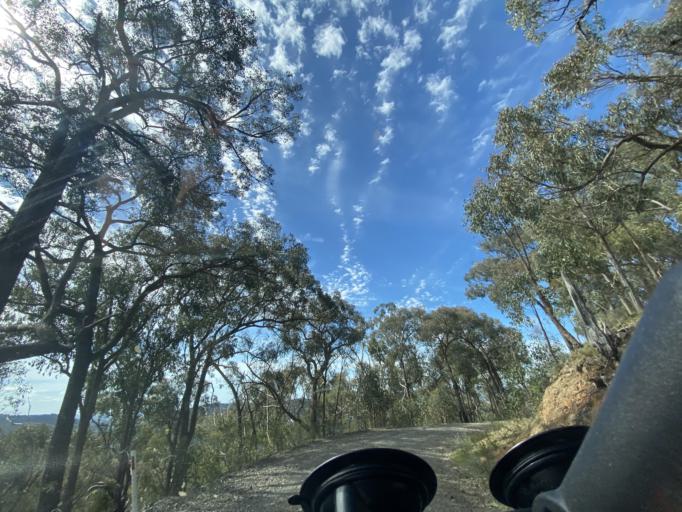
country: AU
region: Victoria
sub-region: Mansfield
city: Mansfield
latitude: -36.8085
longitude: 146.1027
